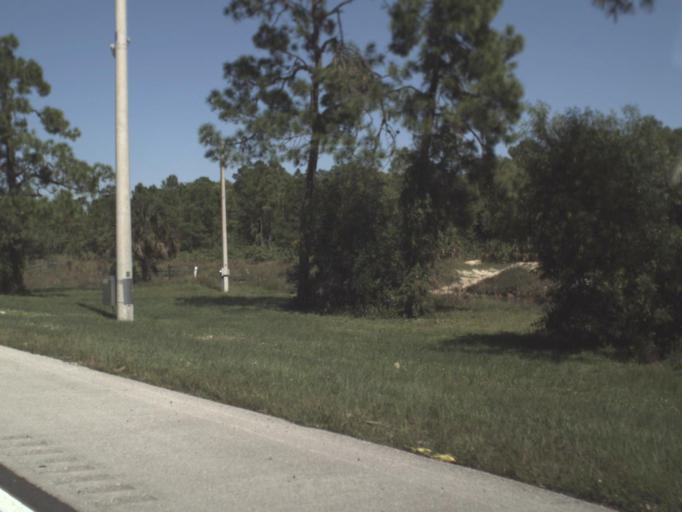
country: US
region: Florida
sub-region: Collier County
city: Vineyards
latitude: 26.1986
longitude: -81.7357
